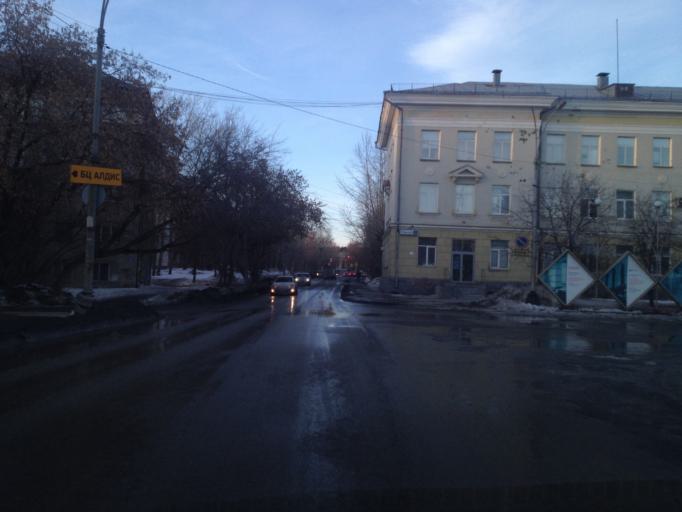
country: RU
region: Sverdlovsk
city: Istok
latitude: 56.7566
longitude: 60.7105
